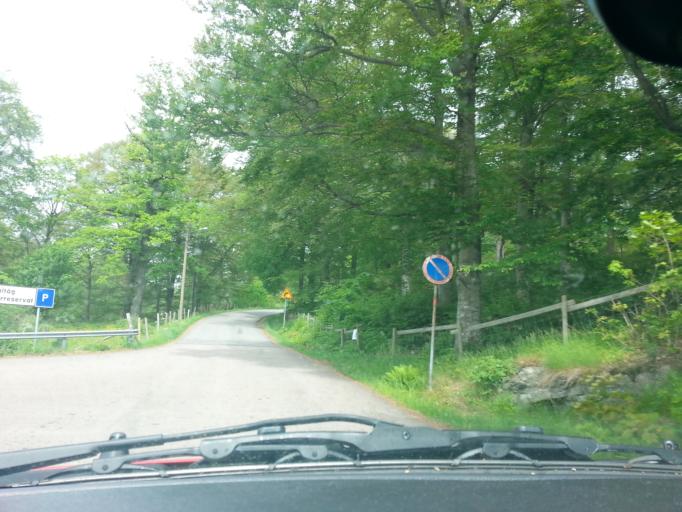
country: SE
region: Vaestra Goetaland
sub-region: Partille Kommun
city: Furulund
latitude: 57.7504
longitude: 12.1753
